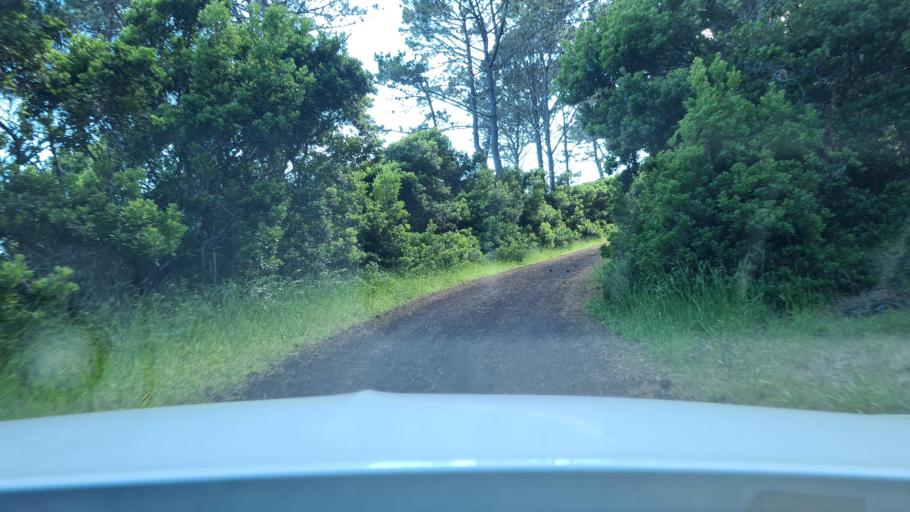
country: PT
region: Azores
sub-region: Sao Roque do Pico
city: Sao Roque do Pico
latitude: 38.4119
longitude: -28.2978
